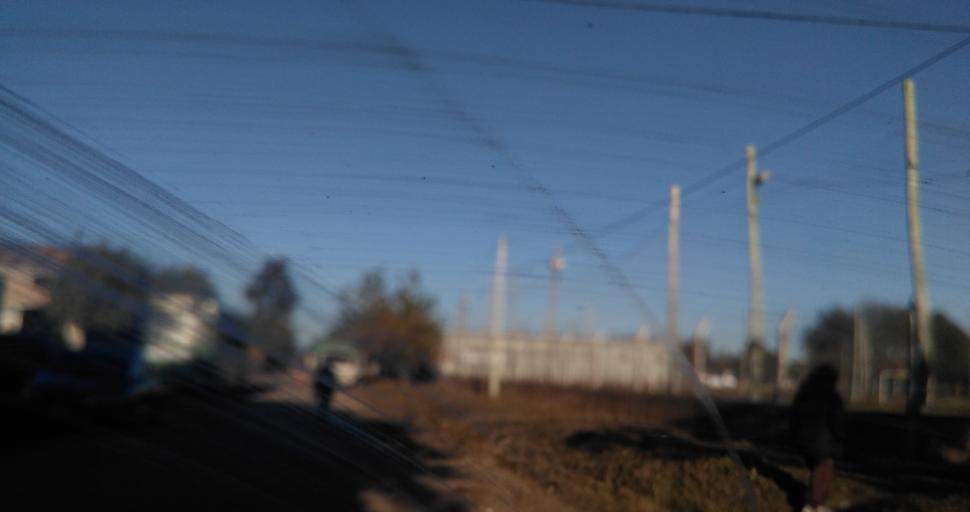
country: AR
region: Chaco
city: Fontana
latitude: -27.4345
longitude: -59.0161
